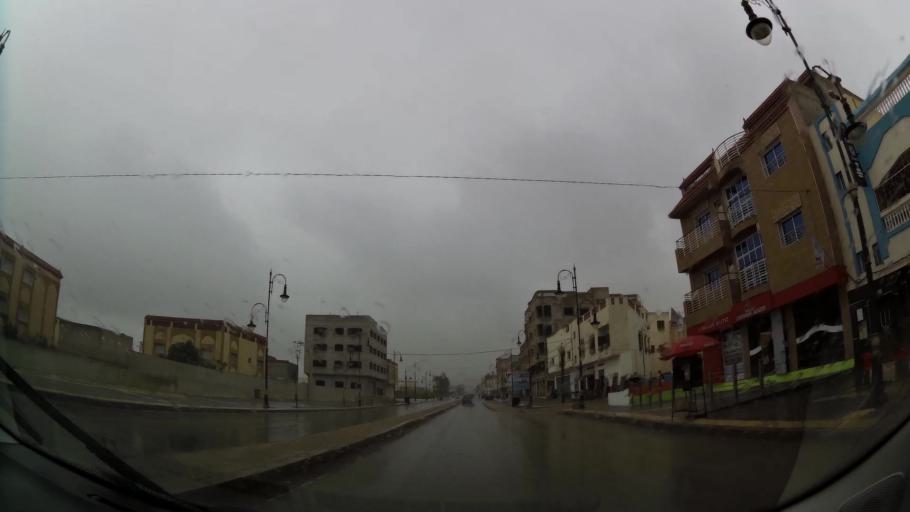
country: MA
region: Taza-Al Hoceima-Taounate
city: Imzourene
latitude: 35.1175
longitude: -3.8420
